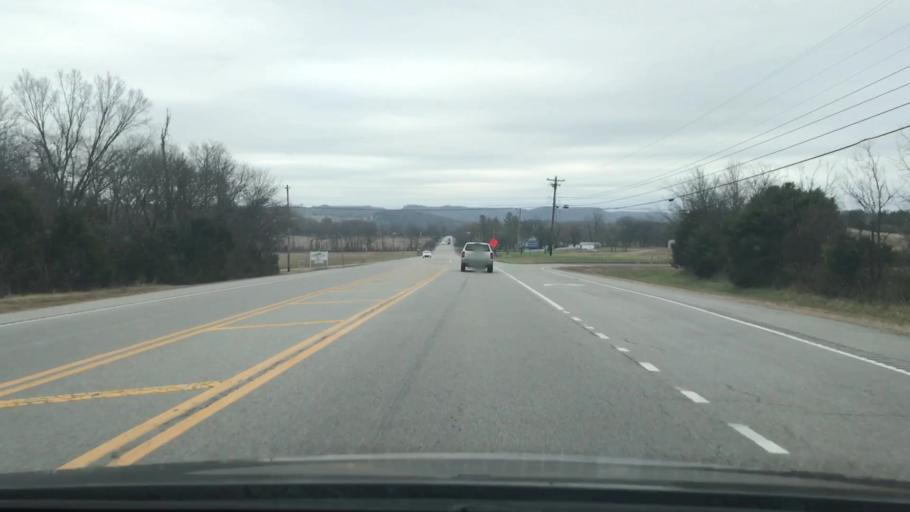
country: US
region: Tennessee
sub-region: Trousdale County
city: Hartsville
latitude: 36.3648
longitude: -86.0748
